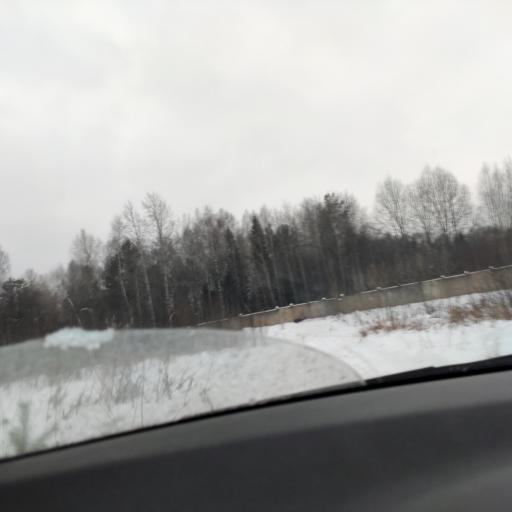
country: RU
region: Perm
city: Overyata
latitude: 58.0435
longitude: 55.8628
